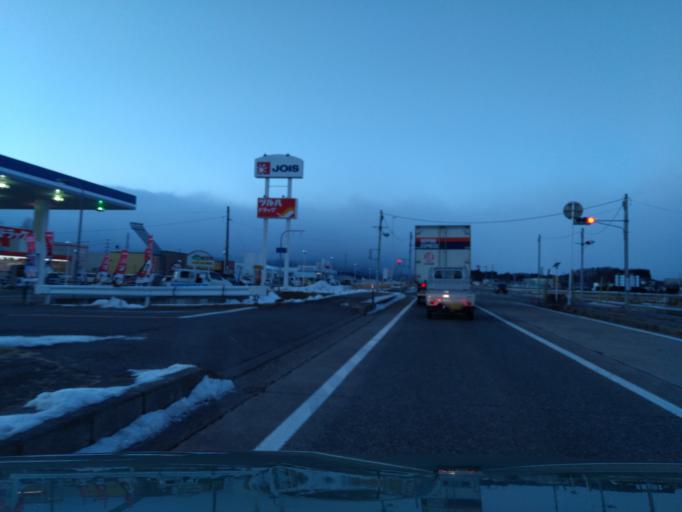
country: JP
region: Iwate
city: Shizukuishi
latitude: 39.6954
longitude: 140.9794
